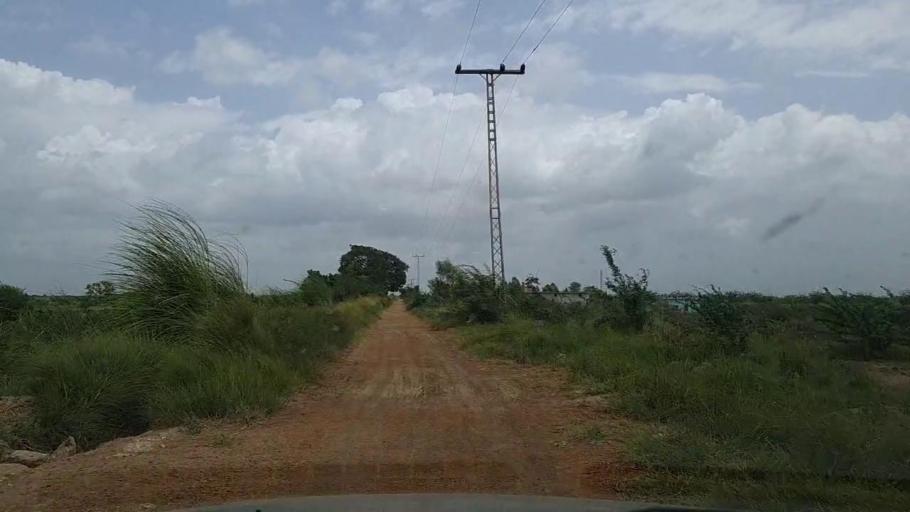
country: PK
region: Sindh
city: Thatta
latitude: 24.6079
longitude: 68.0334
